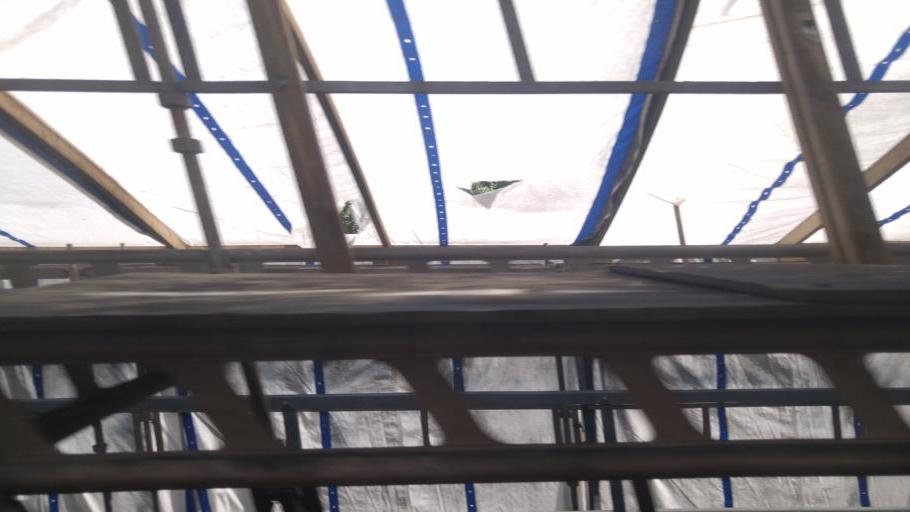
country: NO
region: Sor-Trondelag
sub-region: Midtre Gauldal
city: Storen
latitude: 63.0414
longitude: 10.2933
